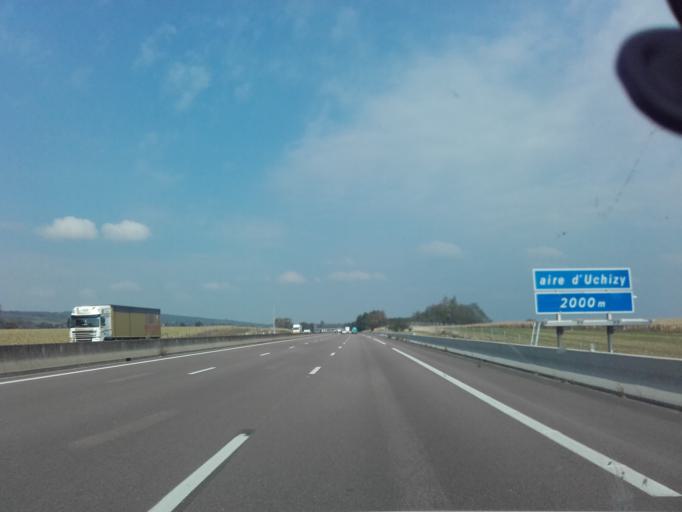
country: FR
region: Rhone-Alpes
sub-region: Departement de l'Ain
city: Pont-de-Vaux
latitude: 46.4862
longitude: 4.8934
